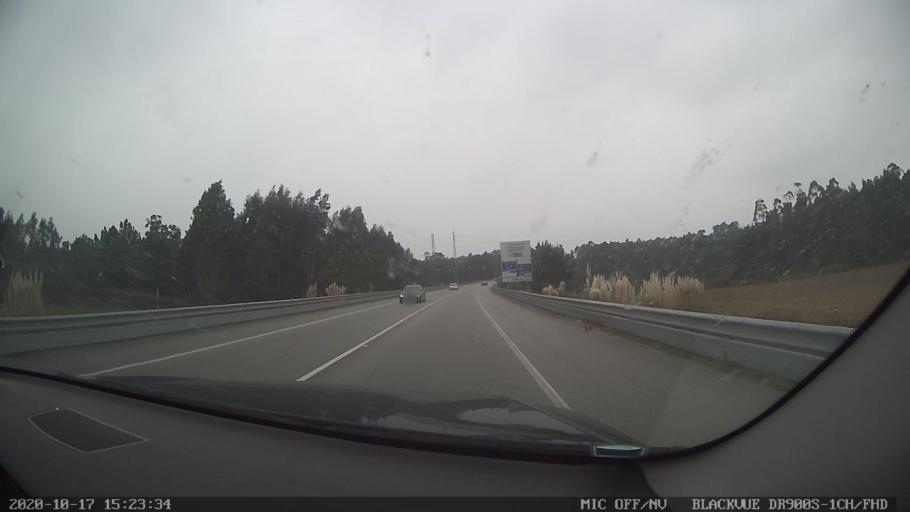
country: PT
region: Braga
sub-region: Esposende
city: Esposende
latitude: 41.5287
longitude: -8.7412
